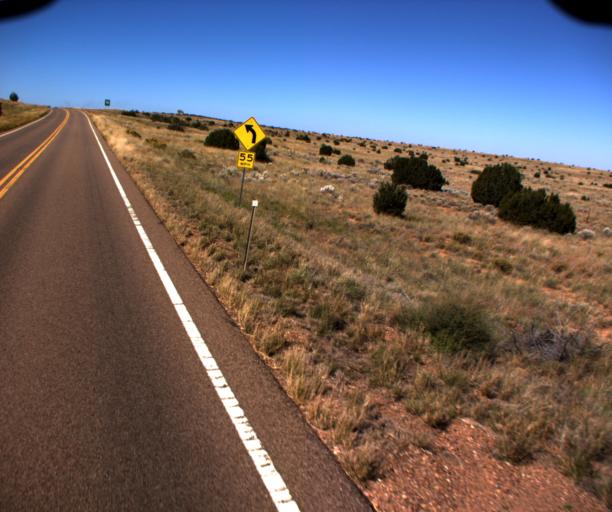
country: US
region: Arizona
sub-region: Navajo County
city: Taylor
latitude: 34.4830
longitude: -110.3301
